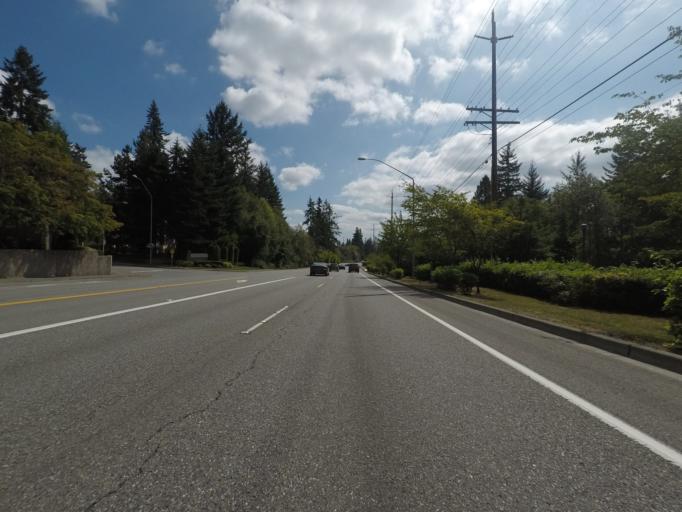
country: US
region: Washington
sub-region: Snohomish County
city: Mill Creek
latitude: 47.8683
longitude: -122.2183
